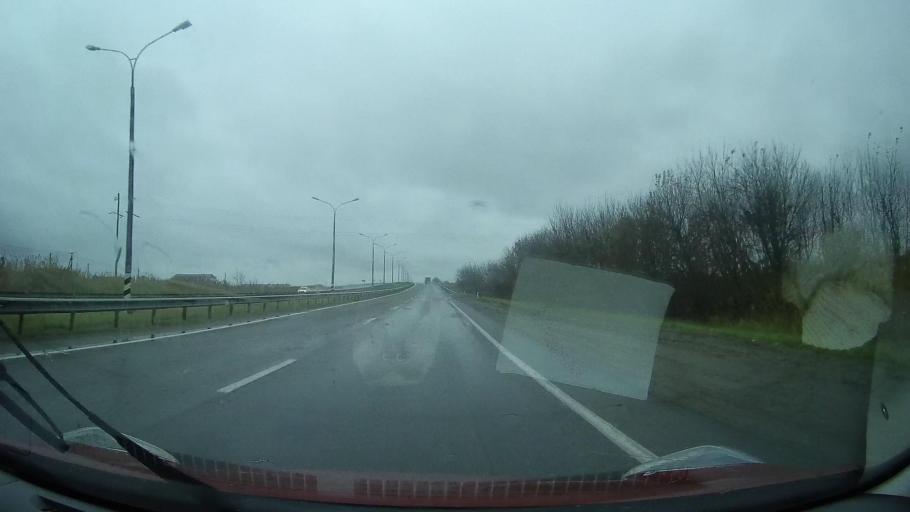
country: RU
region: Stavropol'skiy
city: Nevinnomyssk
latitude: 44.6356
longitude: 41.9993
